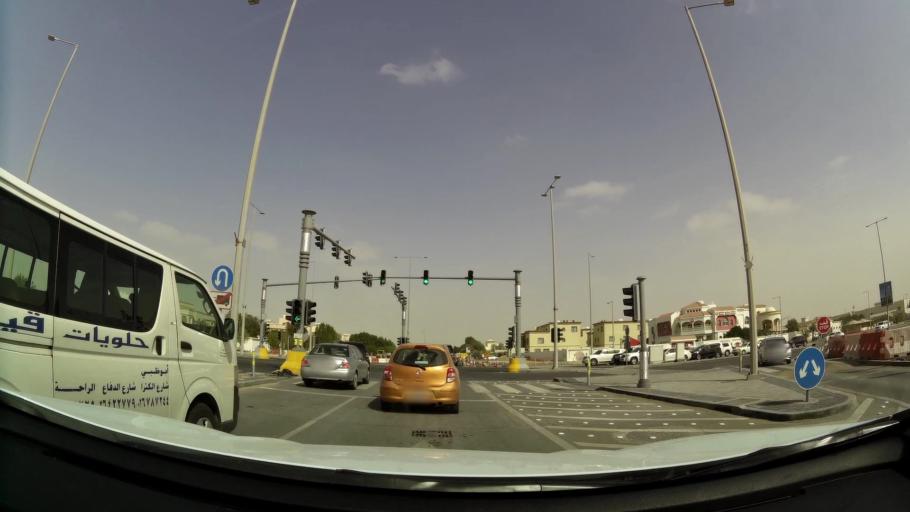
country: AE
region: Abu Dhabi
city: Abu Dhabi
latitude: 24.4191
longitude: 54.5666
